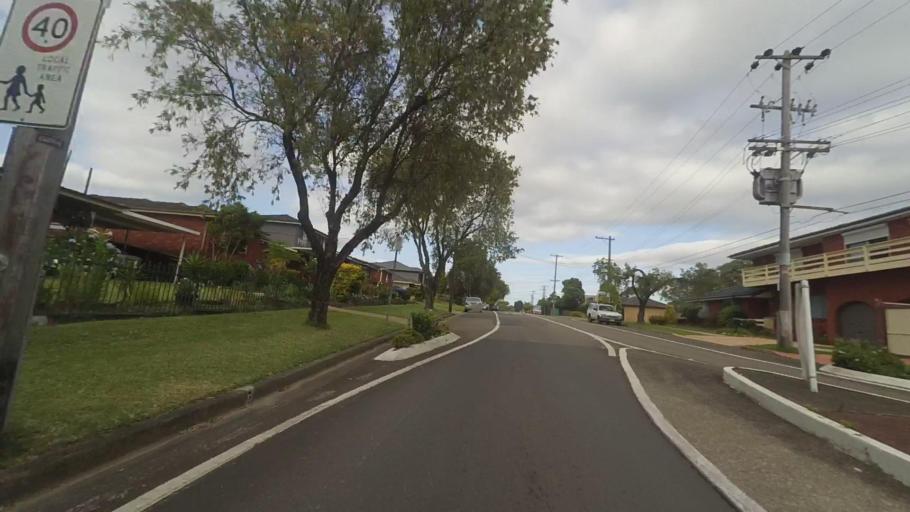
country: AU
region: New South Wales
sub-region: Bankstown
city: Regents Park
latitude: -33.9054
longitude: 150.9908
